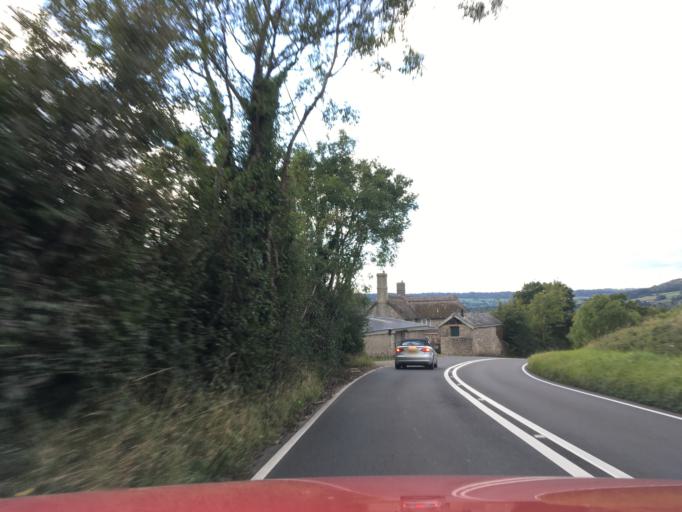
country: GB
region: England
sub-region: Devon
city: Honiton
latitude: 50.7861
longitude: -3.2015
